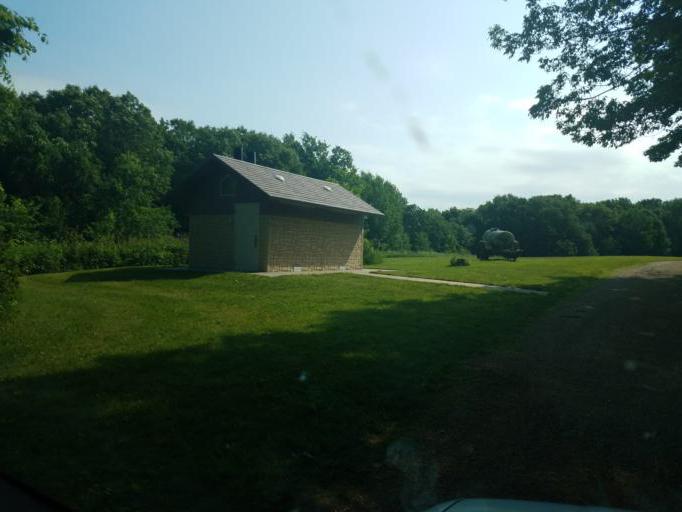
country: US
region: Wisconsin
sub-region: Monroe County
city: Cashton
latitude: 43.7066
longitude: -90.5623
